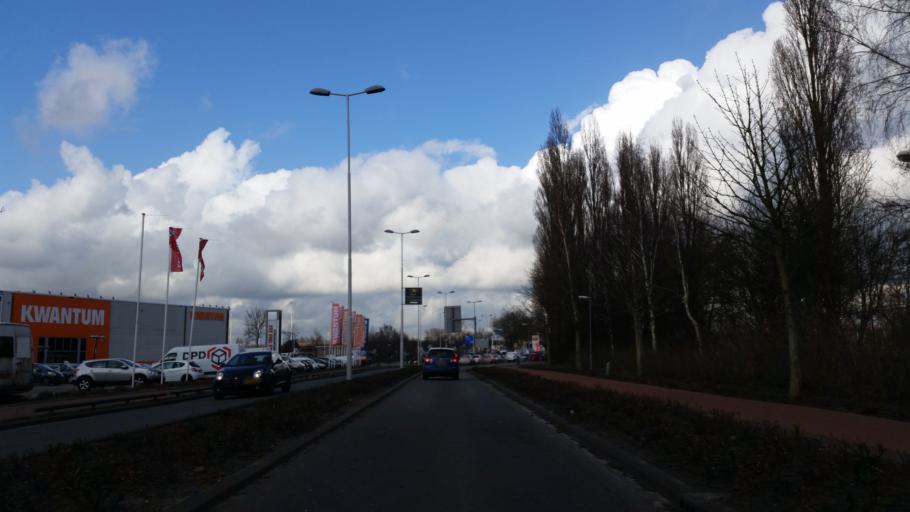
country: NL
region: South Holland
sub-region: Gemeente Rotterdam
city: Delfshaven
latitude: 51.9267
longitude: 4.4384
